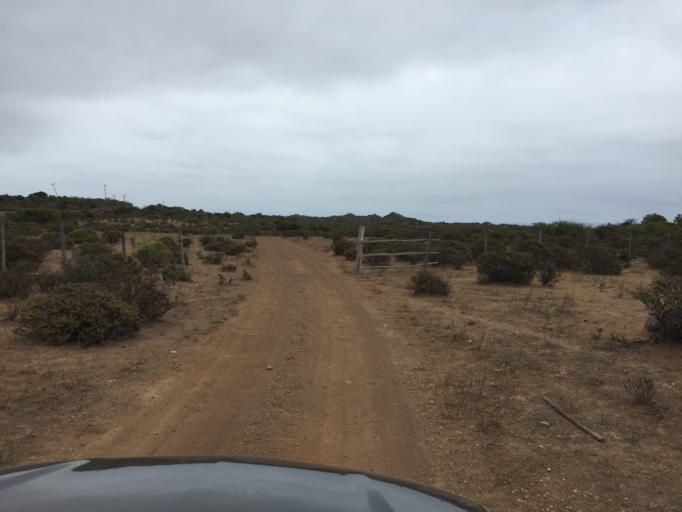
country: CL
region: Valparaiso
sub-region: Petorca Province
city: La Ligua
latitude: -32.1673
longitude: -71.5205
